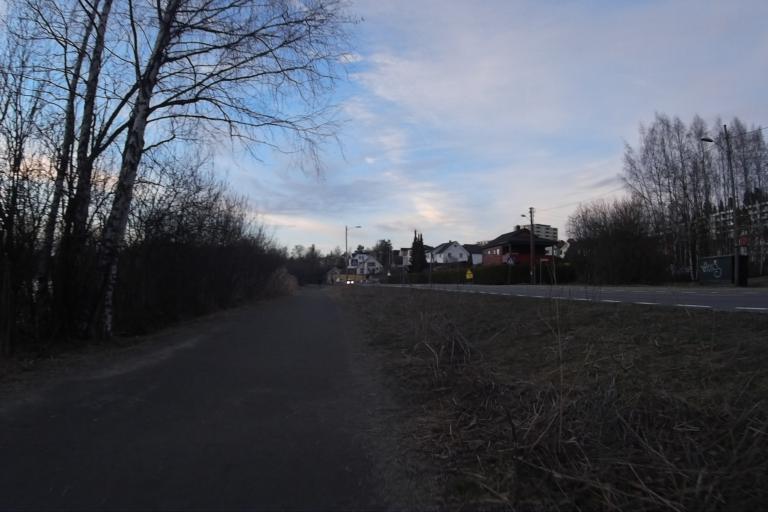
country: NO
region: Oslo
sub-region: Oslo
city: Oslo
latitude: 59.8957
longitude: 10.8326
